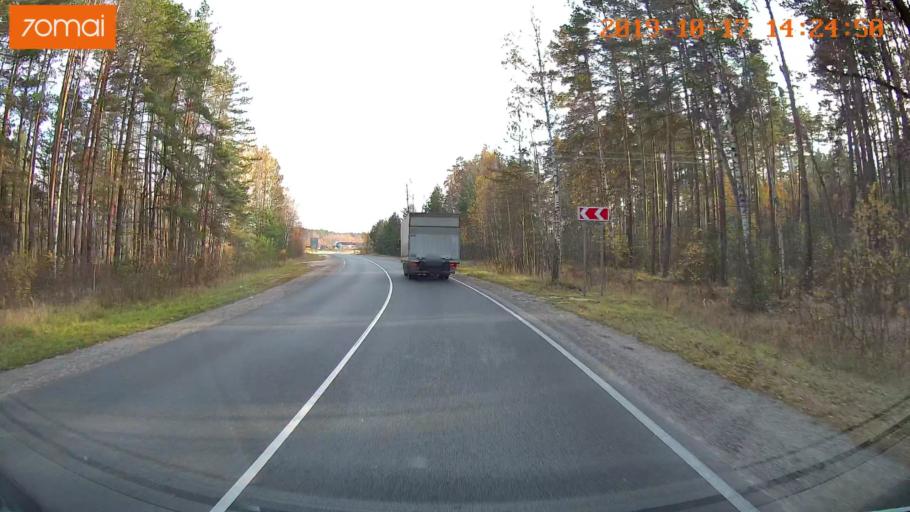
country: RU
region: Moskovskaya
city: Radovitskiy
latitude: 55.0057
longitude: 39.9714
